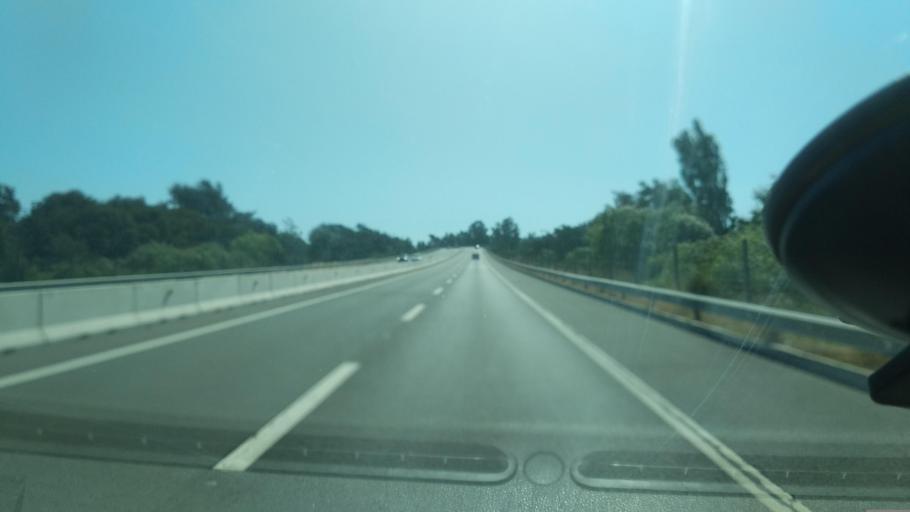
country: CL
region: Valparaiso
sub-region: Provincia de Marga Marga
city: Limache
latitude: -32.9815
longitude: -71.3111
